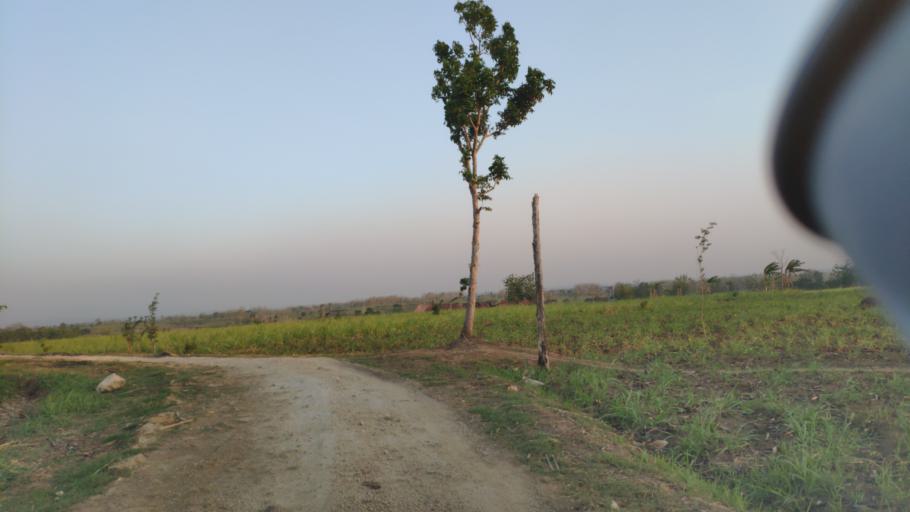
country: ID
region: Central Java
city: Jepang
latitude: -7.0270
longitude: 111.2372
